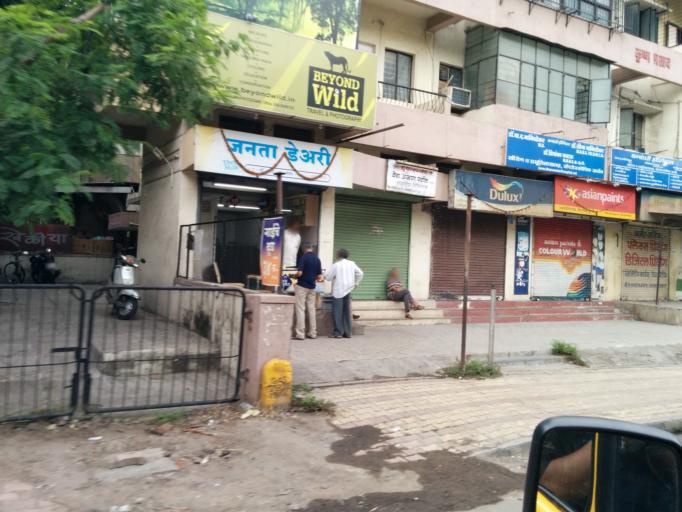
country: IN
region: Maharashtra
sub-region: Pune Division
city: Pune
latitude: 18.5108
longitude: 73.8173
